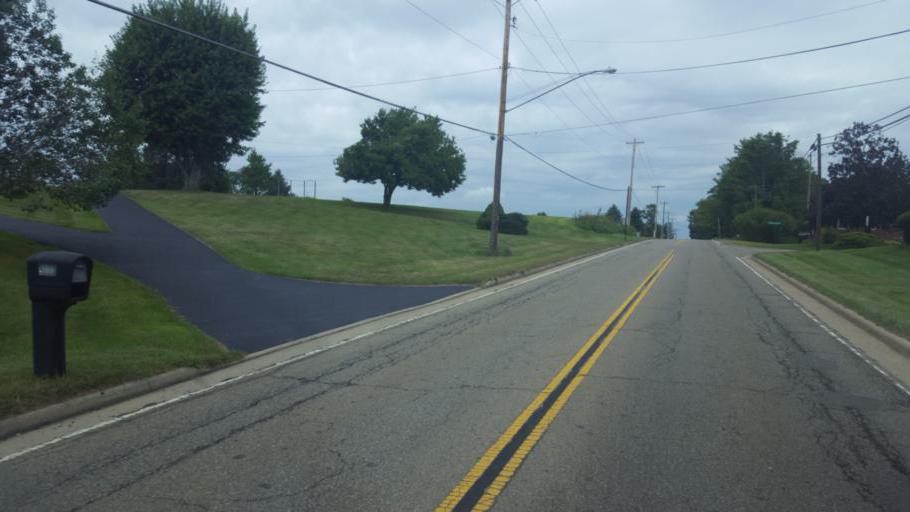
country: US
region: Ohio
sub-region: Knox County
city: Mount Vernon
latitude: 40.4038
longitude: -82.4567
